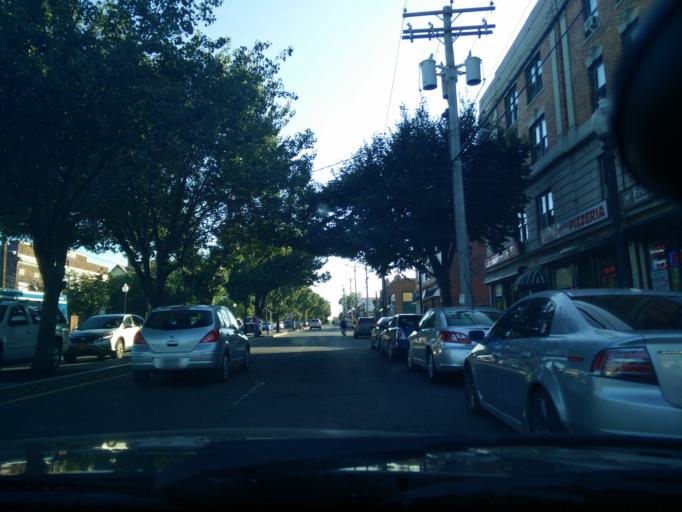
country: US
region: Connecticut
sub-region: Fairfield County
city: Bridgeport
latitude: 41.1640
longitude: -73.2203
